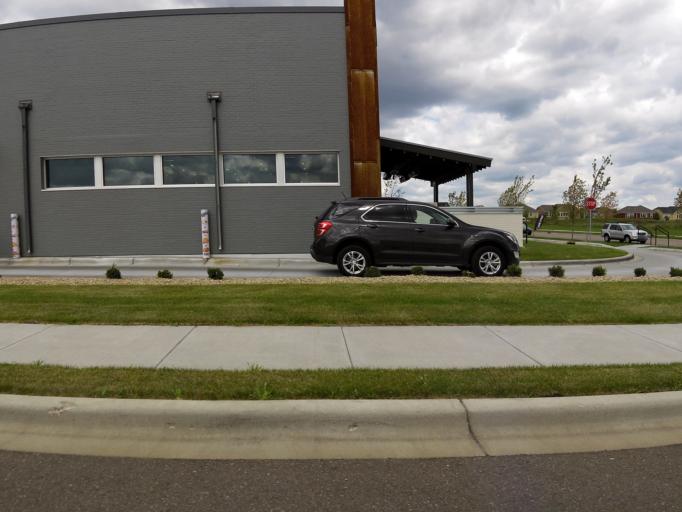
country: US
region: Minnesota
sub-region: Dakota County
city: Apple Valley
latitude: 44.7157
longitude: -93.1720
